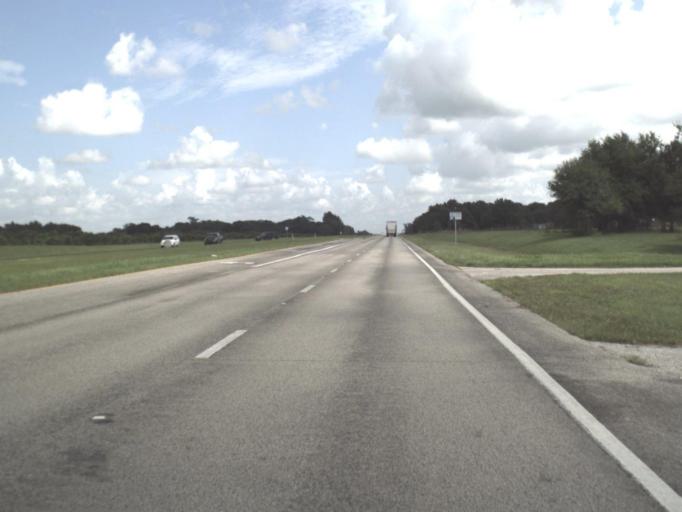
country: US
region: Florida
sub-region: DeSoto County
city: Arcadia
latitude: 27.2883
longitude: -81.8280
